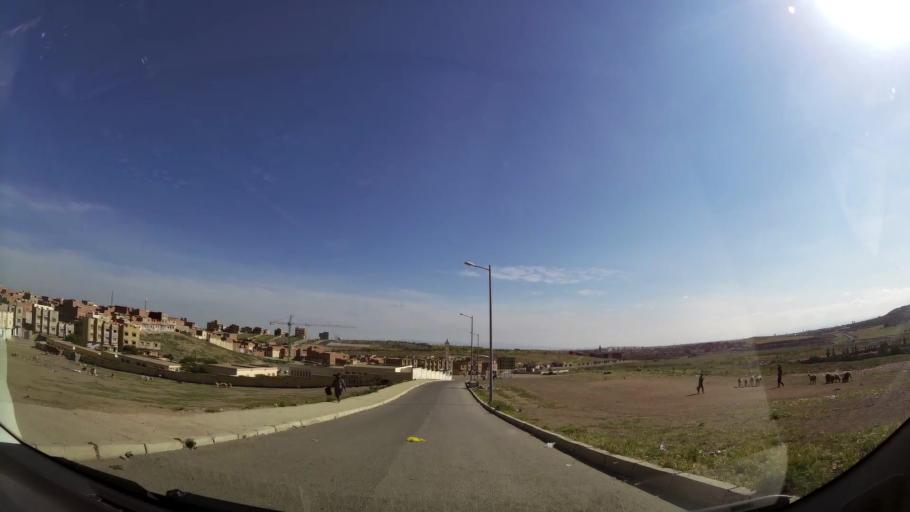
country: MA
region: Oriental
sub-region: Oujda-Angad
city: Oujda
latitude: 34.6475
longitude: -1.9418
